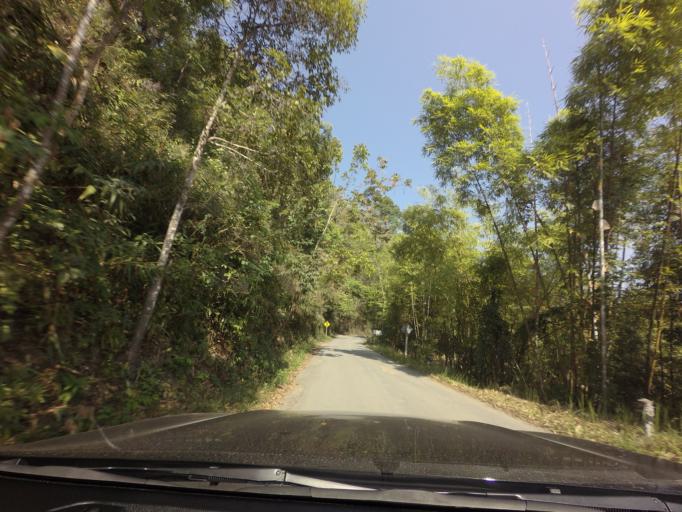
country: TH
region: Kanchanaburi
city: Thong Pha Phum
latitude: 14.6954
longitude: 98.4588
